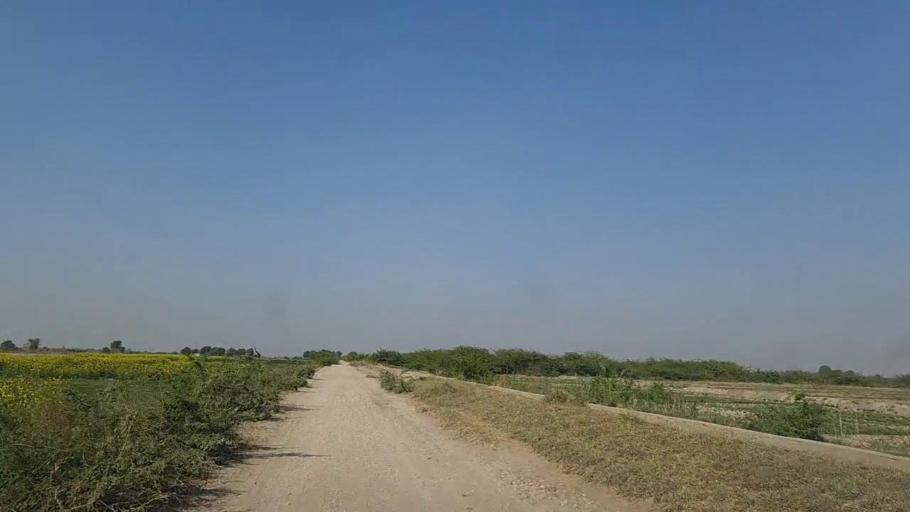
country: PK
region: Sindh
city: Naukot
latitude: 24.9021
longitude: 69.4875
